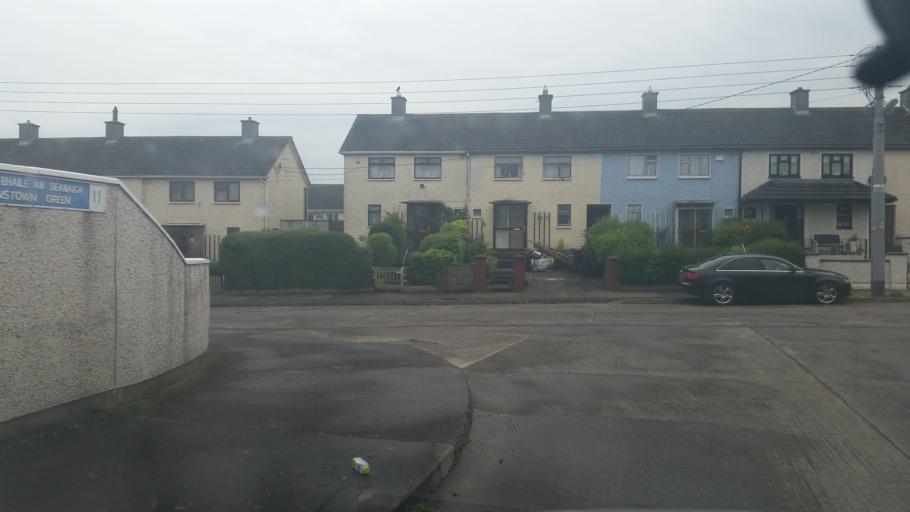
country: IE
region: Leinster
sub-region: Dublin City
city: Finglas
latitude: 53.3853
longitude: -6.3170
